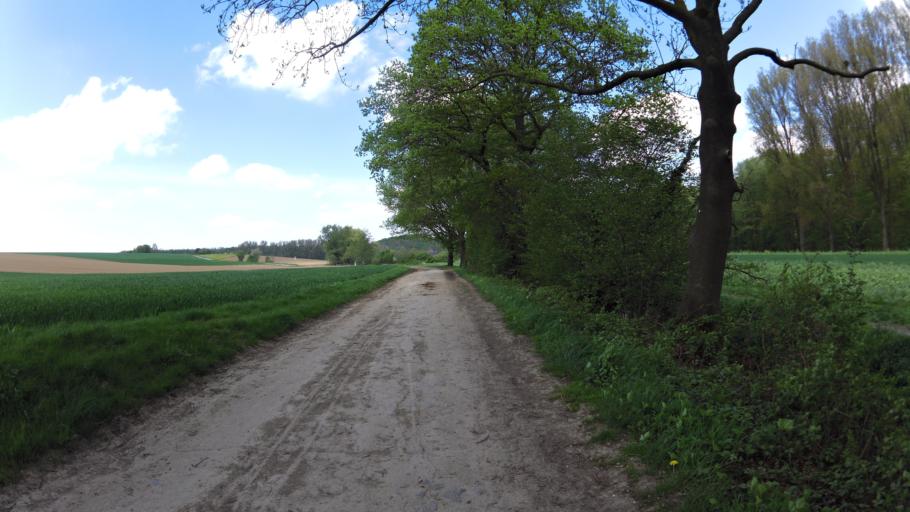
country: NL
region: Limburg
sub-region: Gemeente Kerkrade
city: Kerkrade
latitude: 50.8498
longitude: 6.0563
